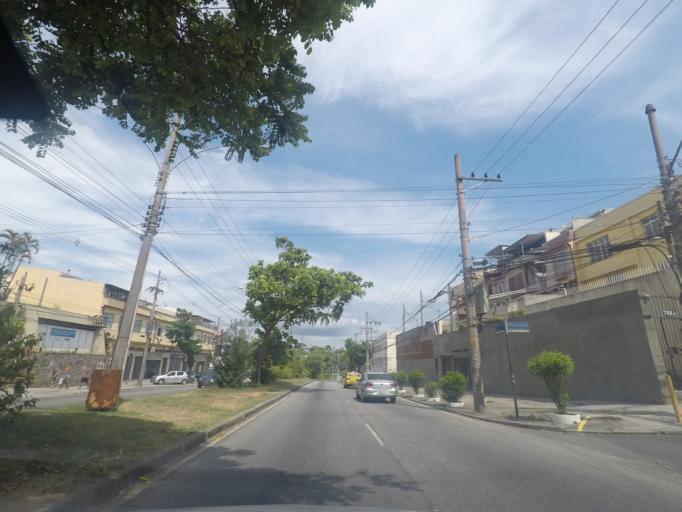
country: BR
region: Rio de Janeiro
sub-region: Rio De Janeiro
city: Rio de Janeiro
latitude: -22.8064
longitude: -43.1992
